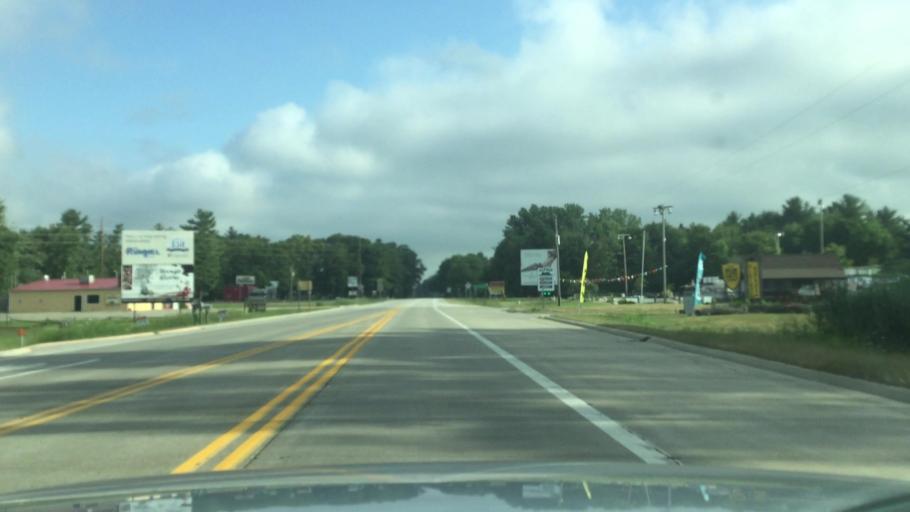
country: US
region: Michigan
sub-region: Saginaw County
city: Birch Run
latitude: 43.2509
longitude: -83.7354
